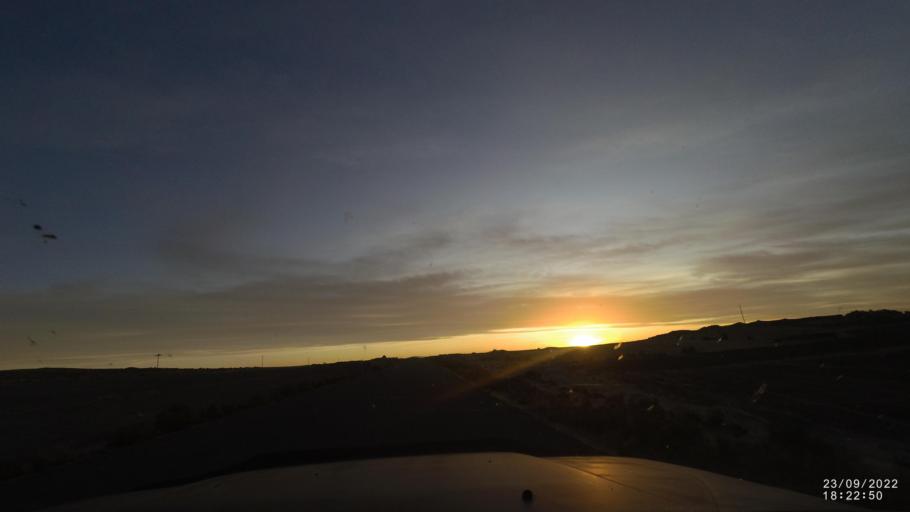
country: BO
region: Oruro
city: Challapata
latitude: -19.2910
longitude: -67.0927
